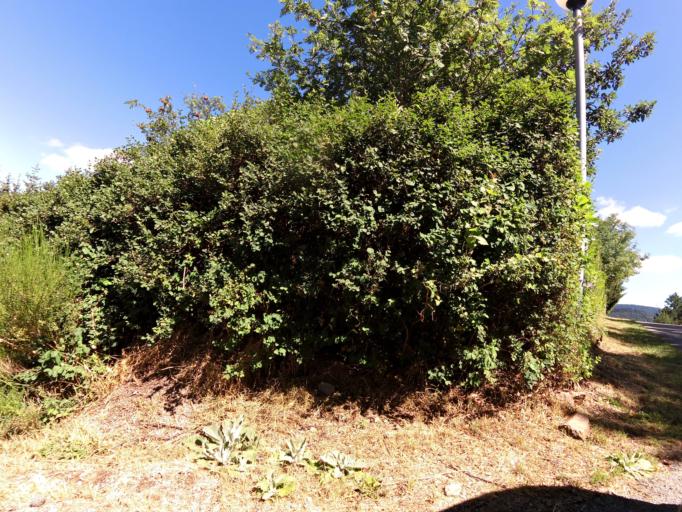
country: FR
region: Languedoc-Roussillon
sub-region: Departement du Gard
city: Valleraugue
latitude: 44.0923
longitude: 3.5489
